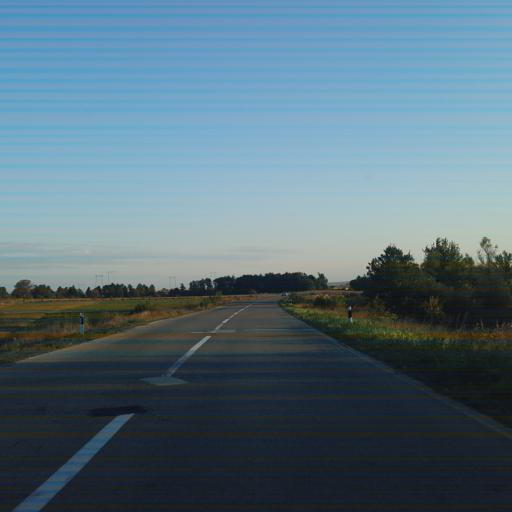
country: RS
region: Central Serbia
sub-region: Borski Okrug
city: Negotin
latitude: 44.1840
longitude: 22.3656
